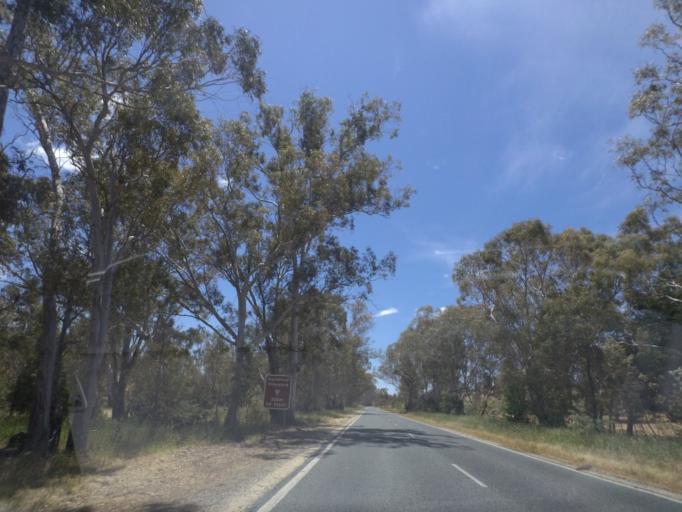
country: AU
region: Victoria
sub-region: Mount Alexander
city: Castlemaine
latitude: -37.1805
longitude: 144.1478
